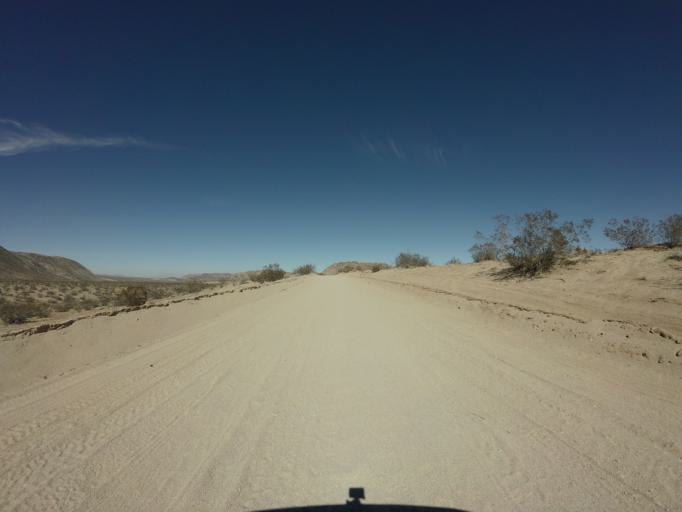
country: US
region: California
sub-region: San Bernardino County
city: Joshua Tree
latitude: 34.3017
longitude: -116.3961
